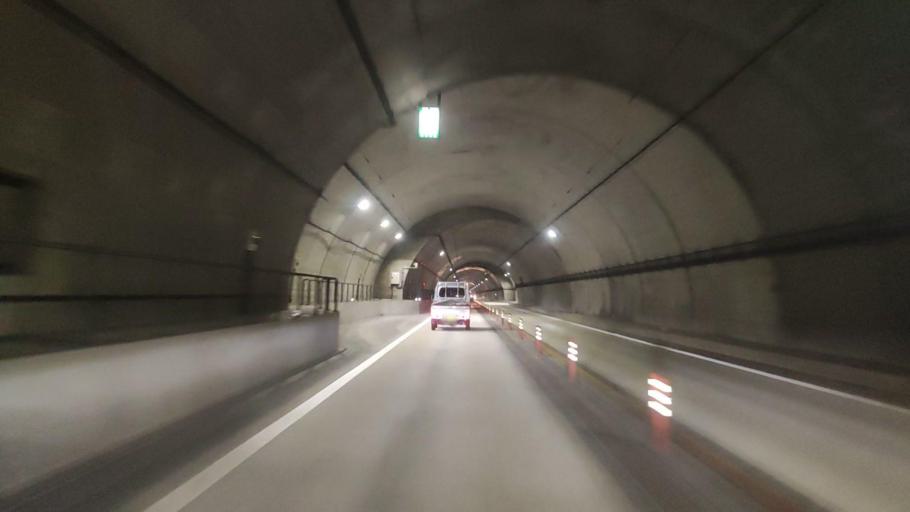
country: JP
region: Wakayama
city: Tanabe
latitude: 33.6157
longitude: 135.4230
